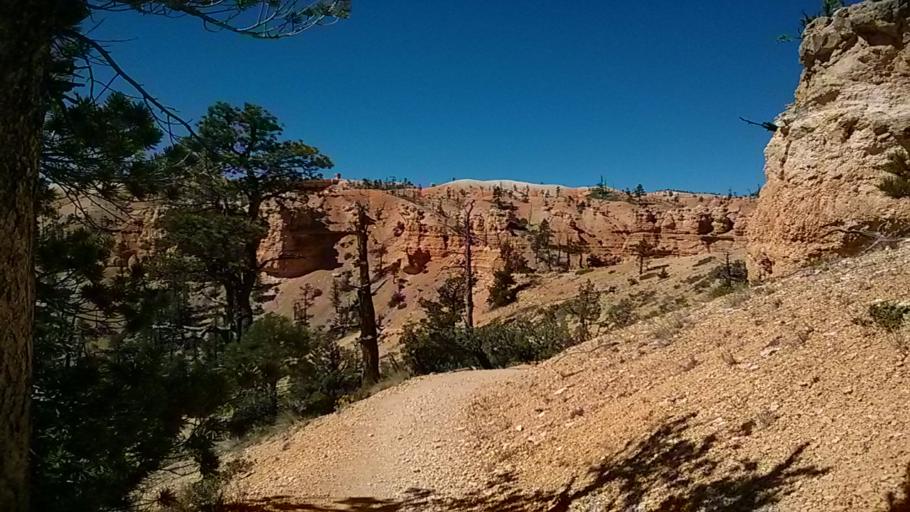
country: US
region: Utah
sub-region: Garfield County
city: Panguitch
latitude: 37.6342
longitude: -112.1448
